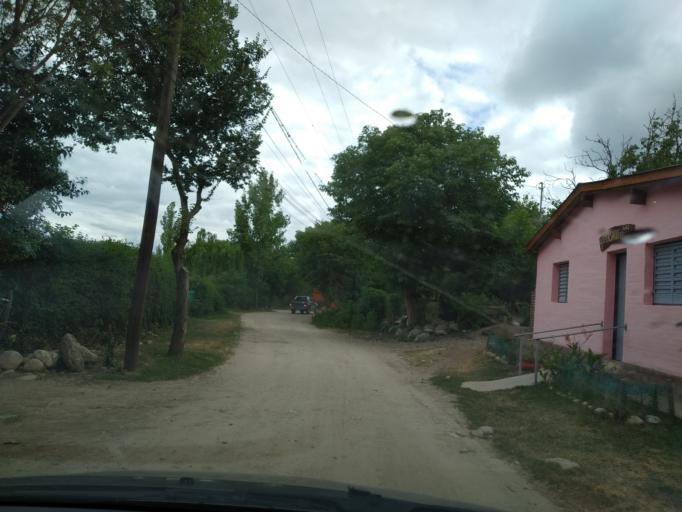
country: AR
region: Cordoba
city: Villa Las Rosas
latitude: -31.9409
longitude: -65.0308
